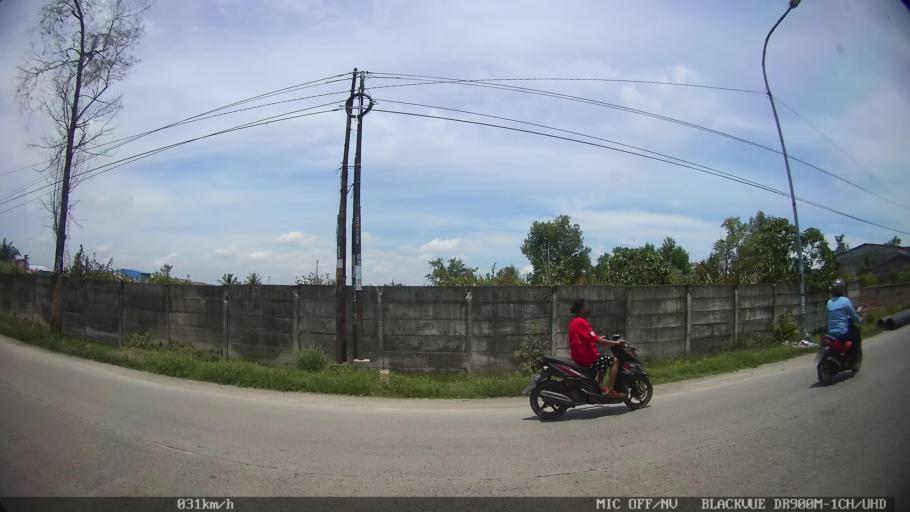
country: ID
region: North Sumatra
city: Belawan
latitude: 3.7590
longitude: 98.6797
